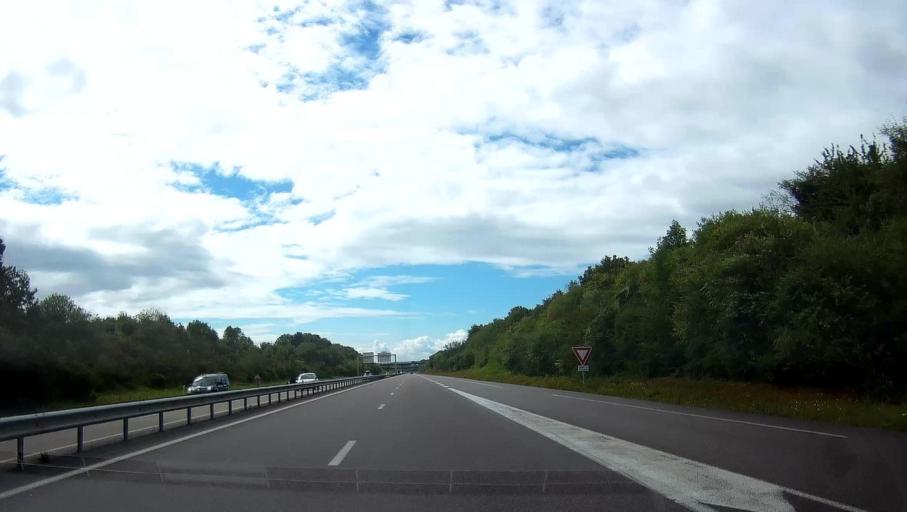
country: FR
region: Champagne-Ardenne
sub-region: Departement de l'Aube
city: Saint-Parres-aux-Tertres
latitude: 48.2903
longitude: 4.1652
